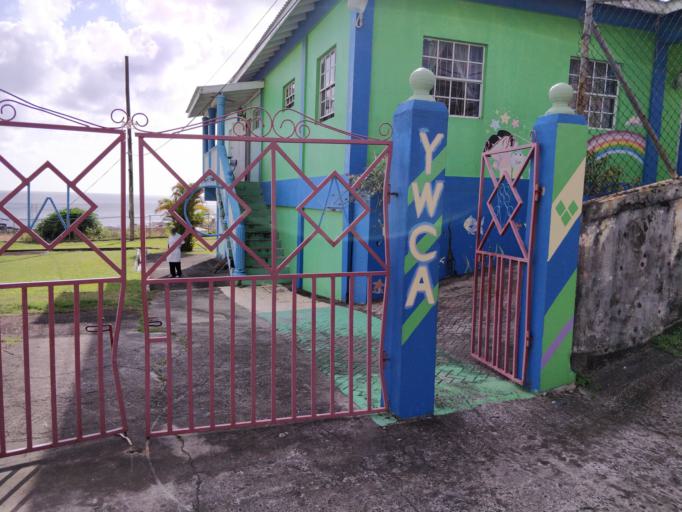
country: VC
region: Saint George
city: Kingstown
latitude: 13.1557
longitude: -61.2234
